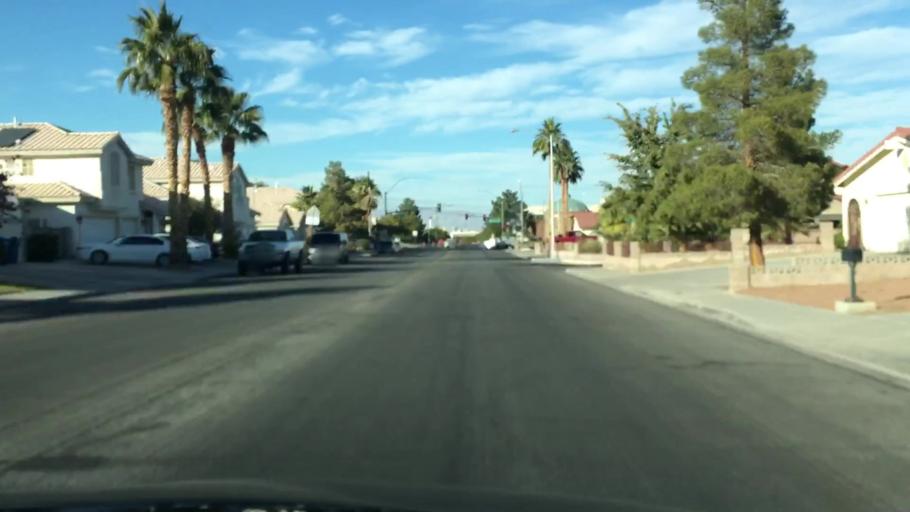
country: US
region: Nevada
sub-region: Clark County
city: Paradise
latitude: 36.0556
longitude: -115.1499
